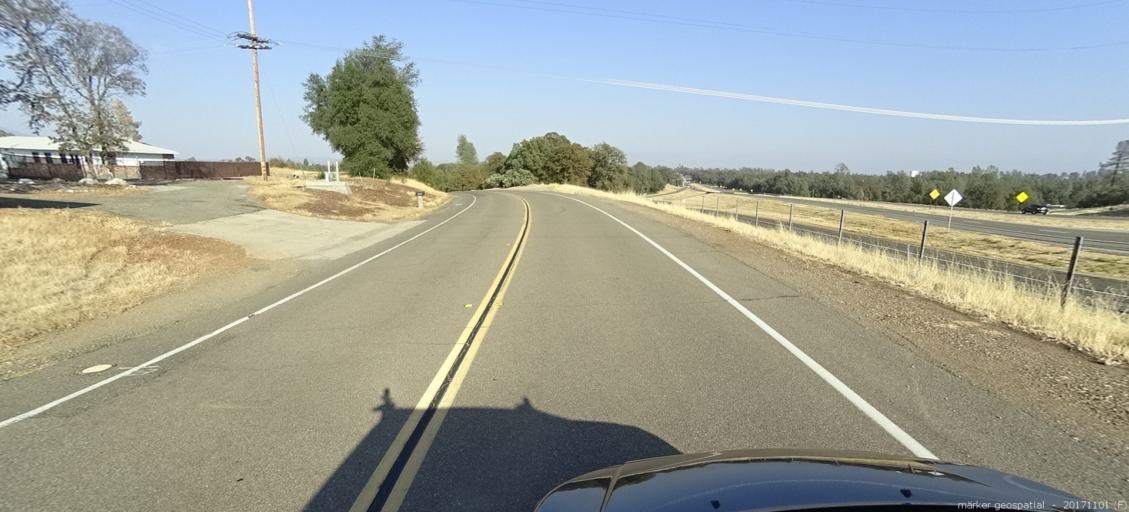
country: US
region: California
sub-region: Shasta County
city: Redding
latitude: 40.6203
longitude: -122.3232
